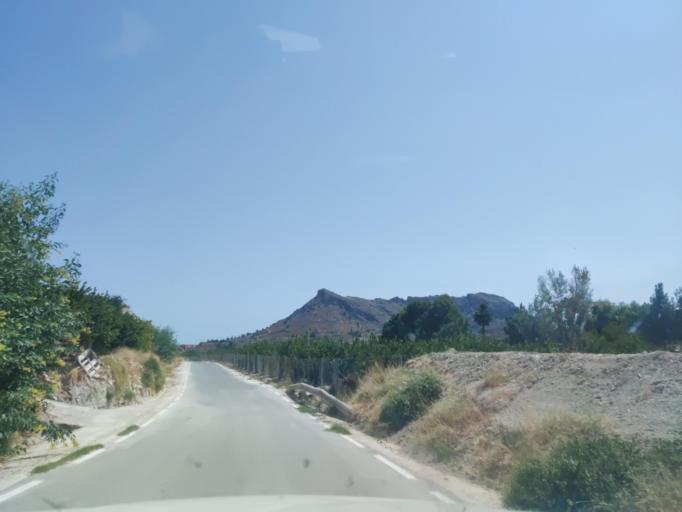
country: ES
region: Murcia
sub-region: Murcia
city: Ulea
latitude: 38.1386
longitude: -1.3184
